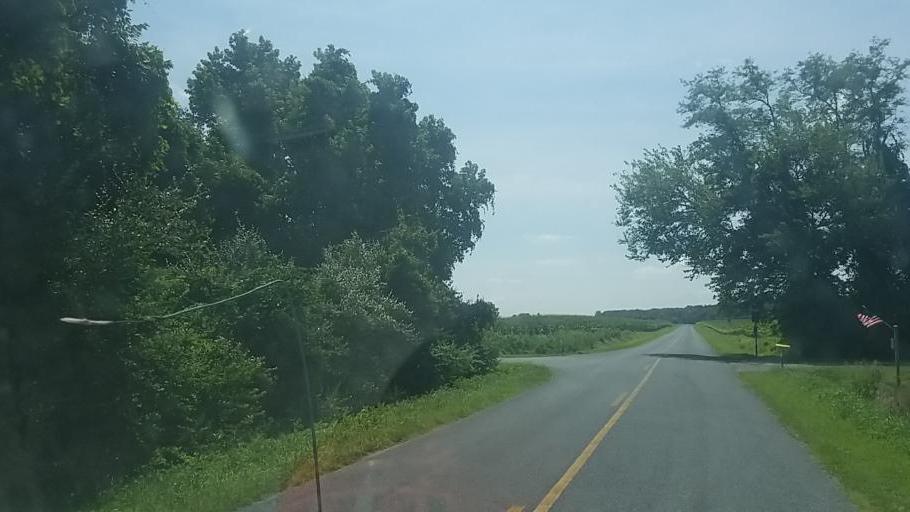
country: US
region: Maryland
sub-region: Caroline County
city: Ridgely
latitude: 38.9016
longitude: -75.9336
